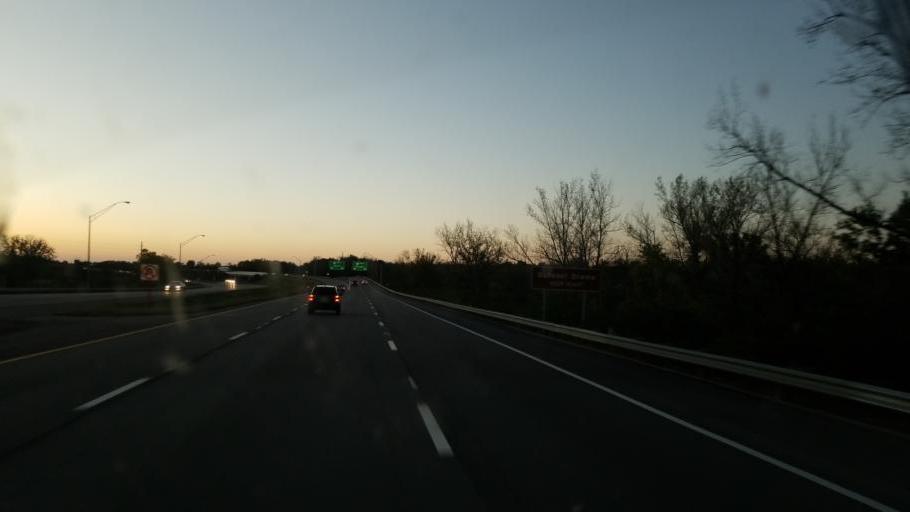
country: US
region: Ohio
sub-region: Ross County
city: Chillicothe
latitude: 39.3470
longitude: -82.9579
